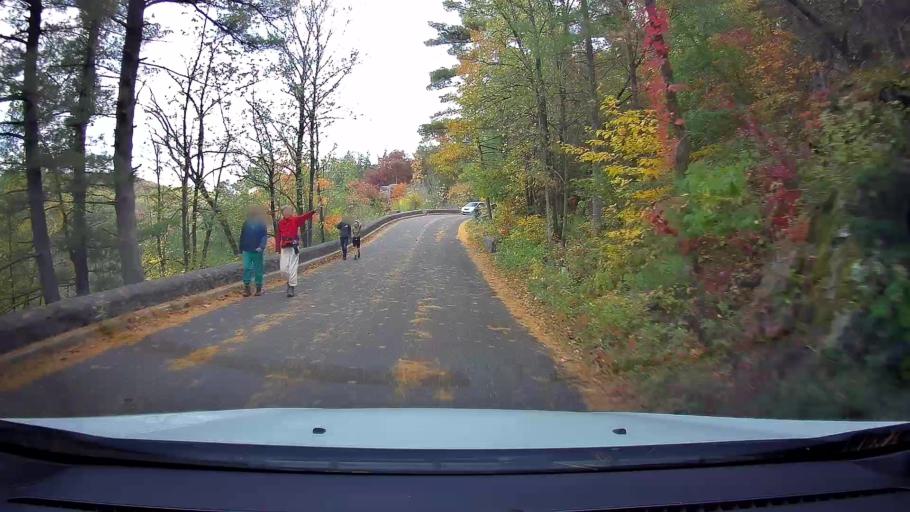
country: US
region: Wisconsin
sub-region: Polk County
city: Saint Croix Falls
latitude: 45.3980
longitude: -92.6494
